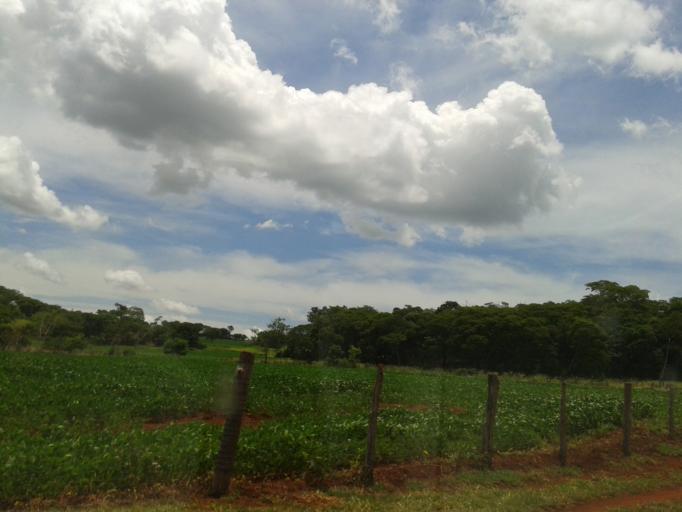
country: BR
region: Minas Gerais
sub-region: Centralina
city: Centralina
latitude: -18.7007
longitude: -49.2292
